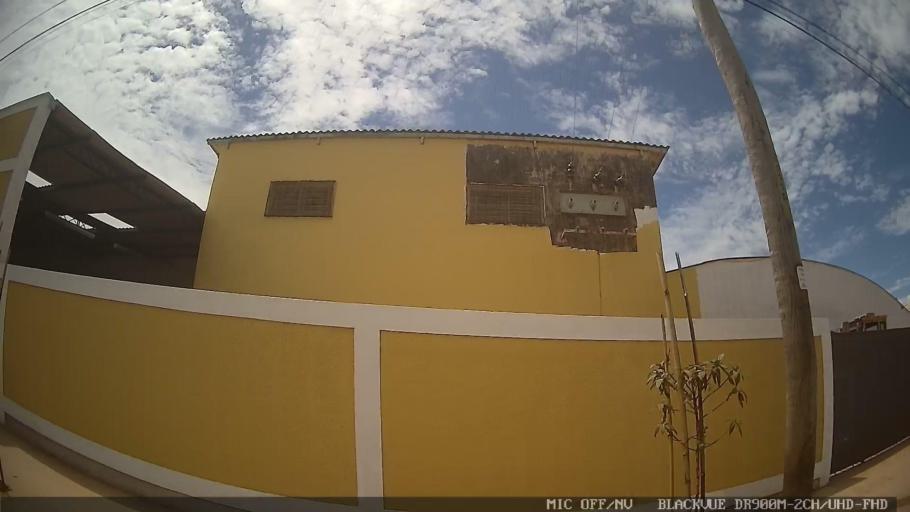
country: BR
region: Sao Paulo
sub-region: Conchas
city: Conchas
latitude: -23.0868
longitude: -47.9787
